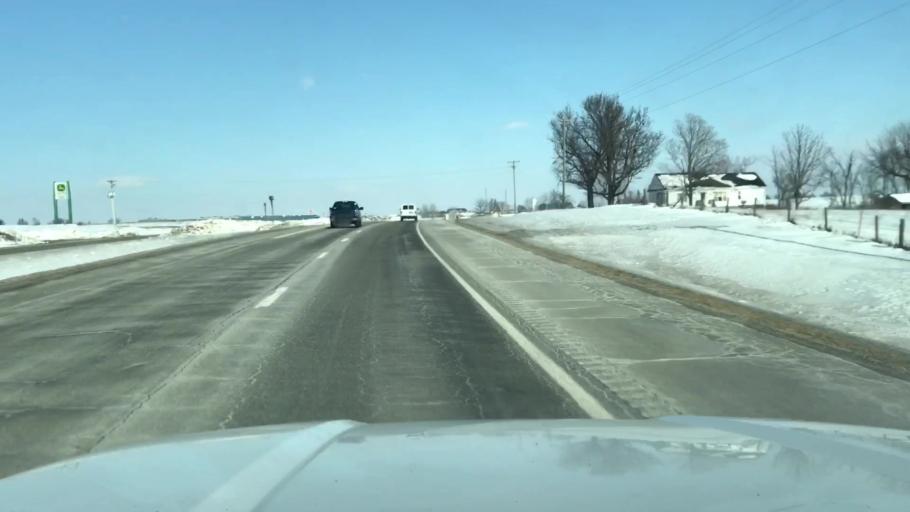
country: US
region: Missouri
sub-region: Nodaway County
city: Maryville
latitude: 40.2986
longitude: -94.8748
